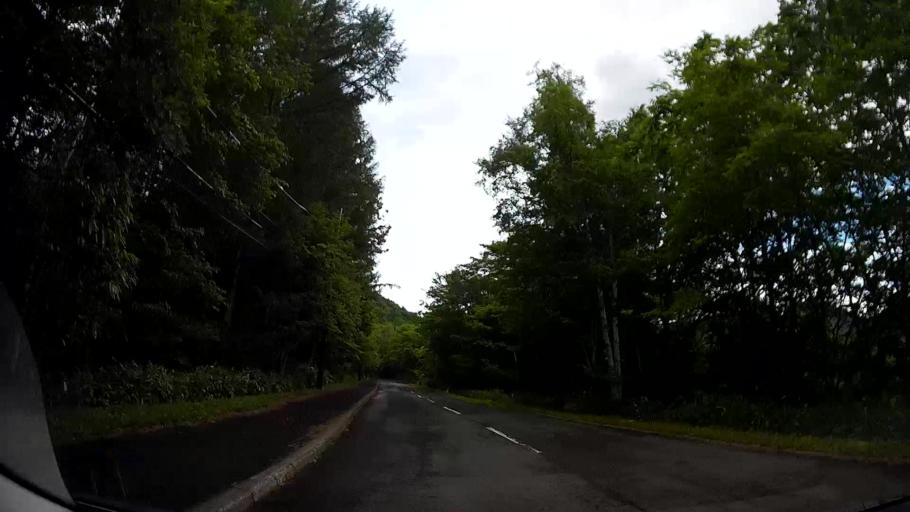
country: JP
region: Hokkaido
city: Sapporo
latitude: 42.9415
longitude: 141.1536
